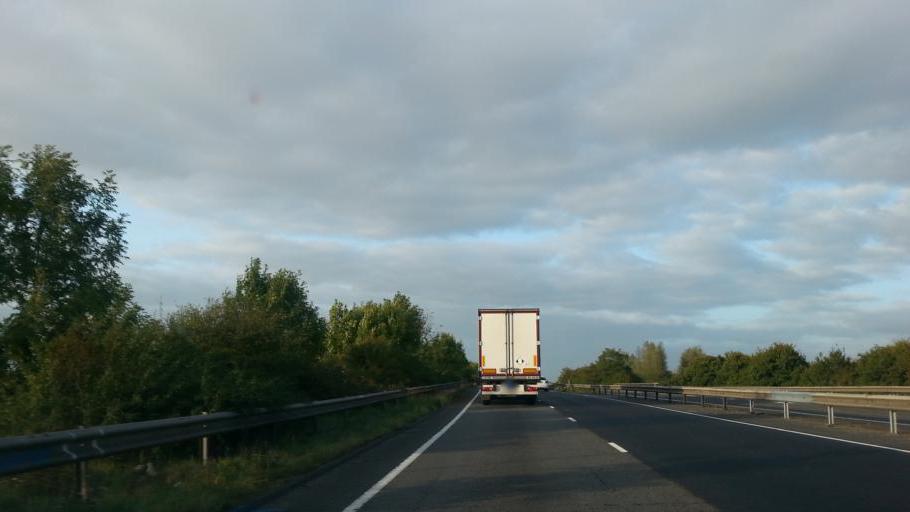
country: GB
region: England
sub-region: Oxfordshire
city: Yarnton
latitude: 51.7931
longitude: -1.2870
